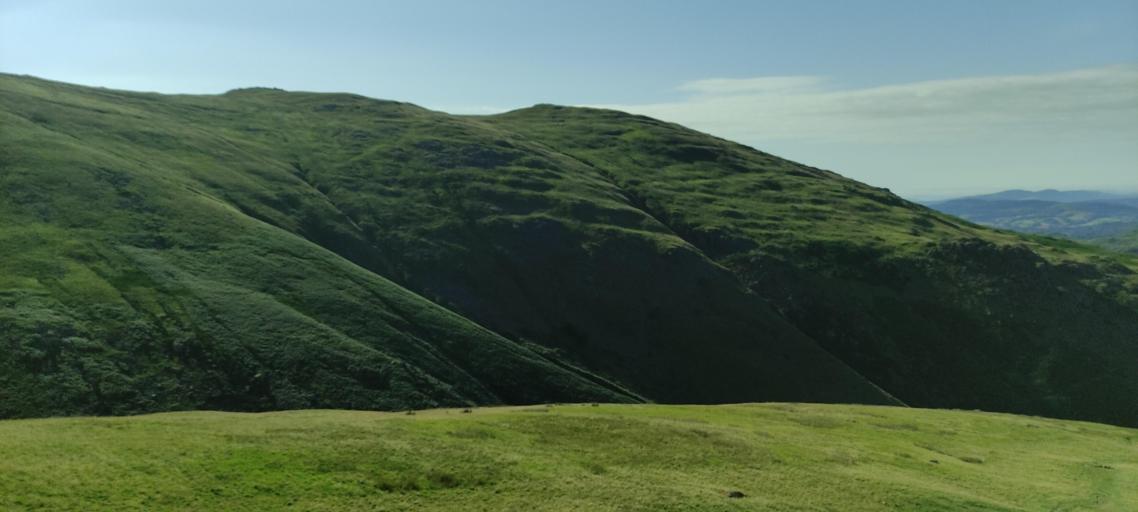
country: GB
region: England
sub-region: Cumbria
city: Ambleside
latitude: 54.4740
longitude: -3.0078
